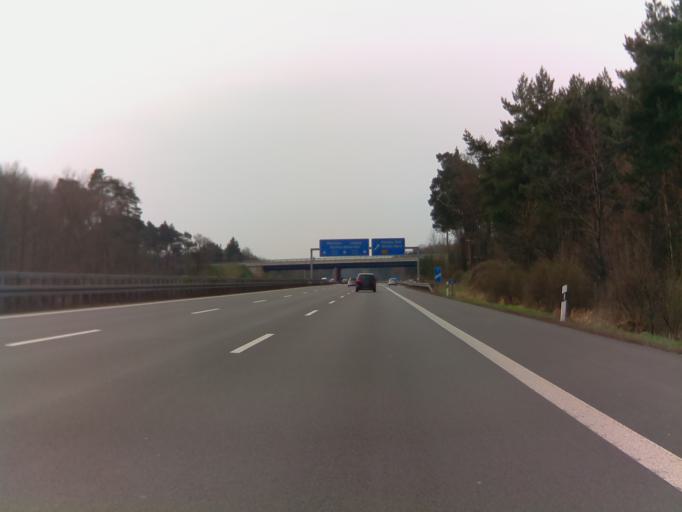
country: DE
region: Saxony-Anhalt
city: Raguhn
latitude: 51.7550
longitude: 12.2299
